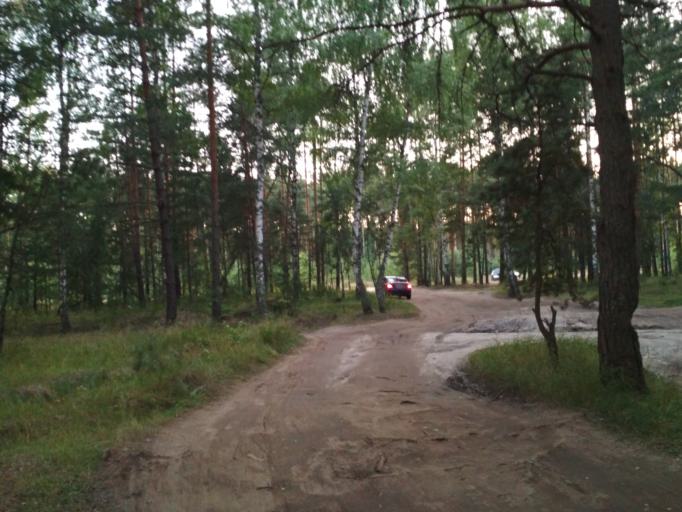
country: RU
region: Rjazan
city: Solotcha
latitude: 54.8261
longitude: 39.9483
